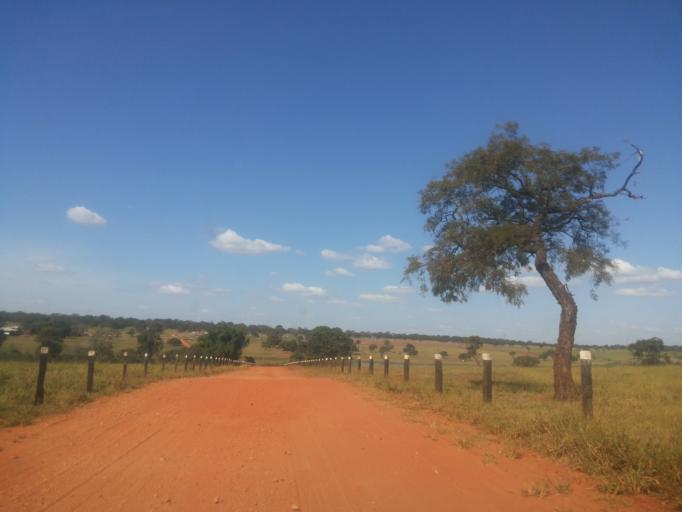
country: BR
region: Minas Gerais
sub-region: Santa Vitoria
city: Santa Vitoria
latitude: -19.0079
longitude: -50.4197
